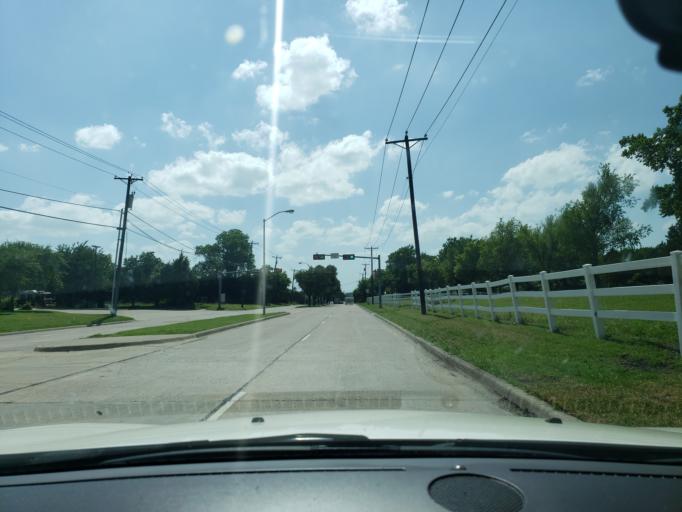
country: US
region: Texas
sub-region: Dallas County
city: Rowlett
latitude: 32.8939
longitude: -96.5647
